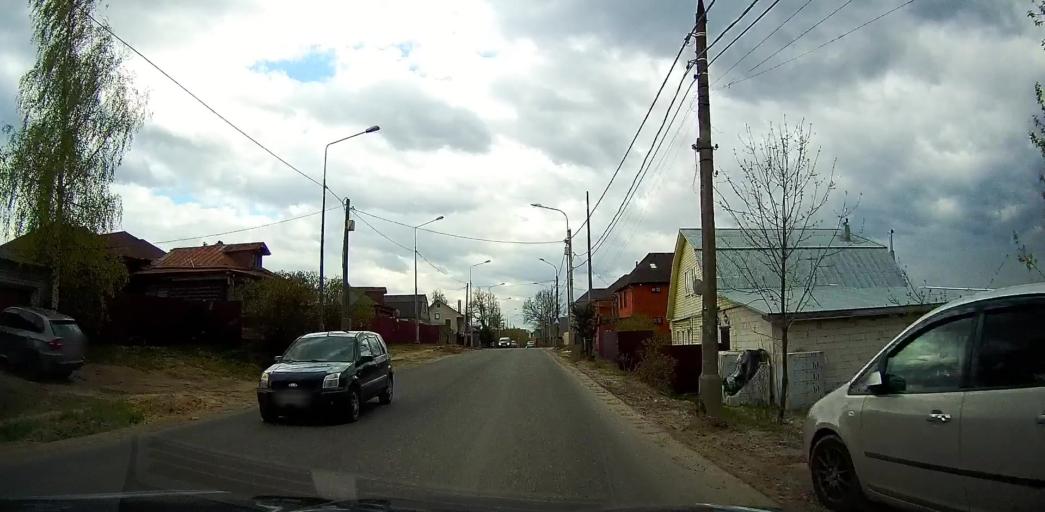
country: RU
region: Moskovskaya
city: Pavlovskiy Posad
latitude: 55.7933
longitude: 38.6868
